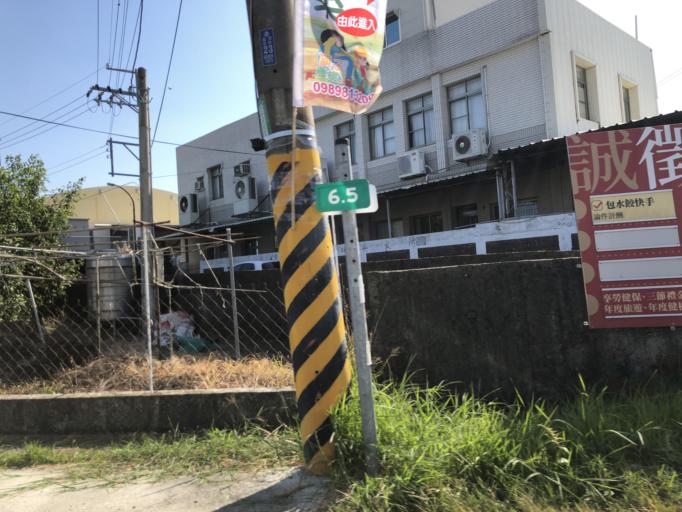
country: TW
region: Taiwan
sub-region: Tainan
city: Tainan
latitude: 23.0305
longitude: 120.2955
